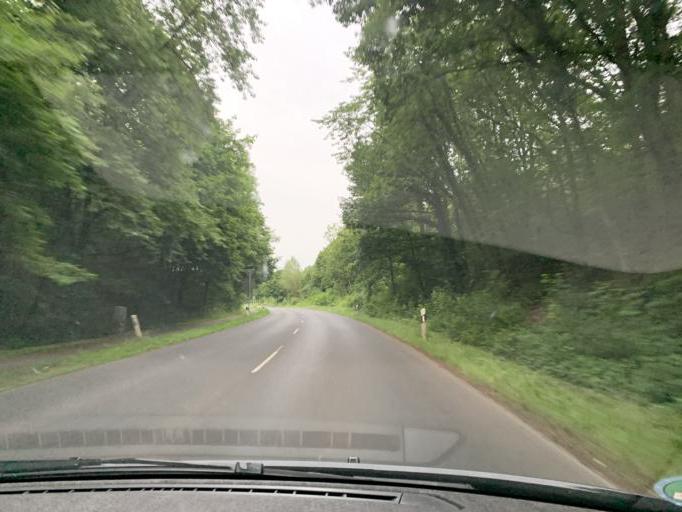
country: DE
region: North Rhine-Westphalia
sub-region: Regierungsbezirk Koln
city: Kerpen
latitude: 50.8961
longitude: 6.7171
